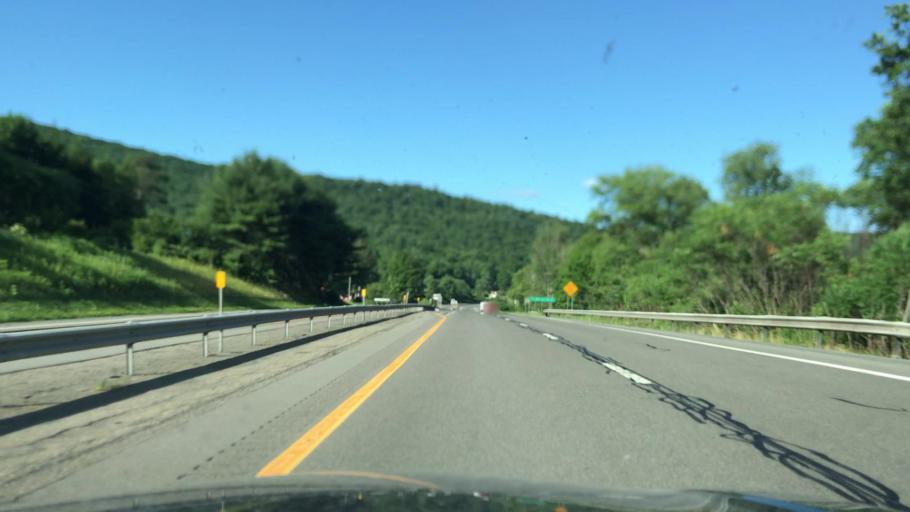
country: US
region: New York
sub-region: Broome County
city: Deposit
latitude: 42.0059
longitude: -75.3745
